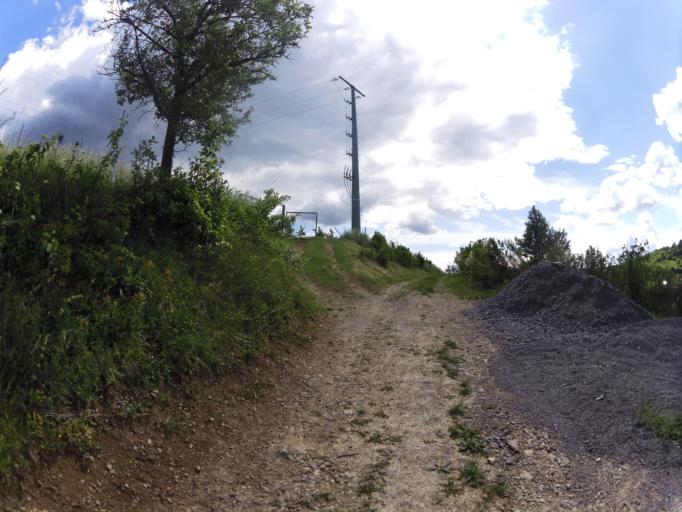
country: DE
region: Bavaria
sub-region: Regierungsbezirk Unterfranken
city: Zellingen
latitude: 49.8705
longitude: 9.8025
